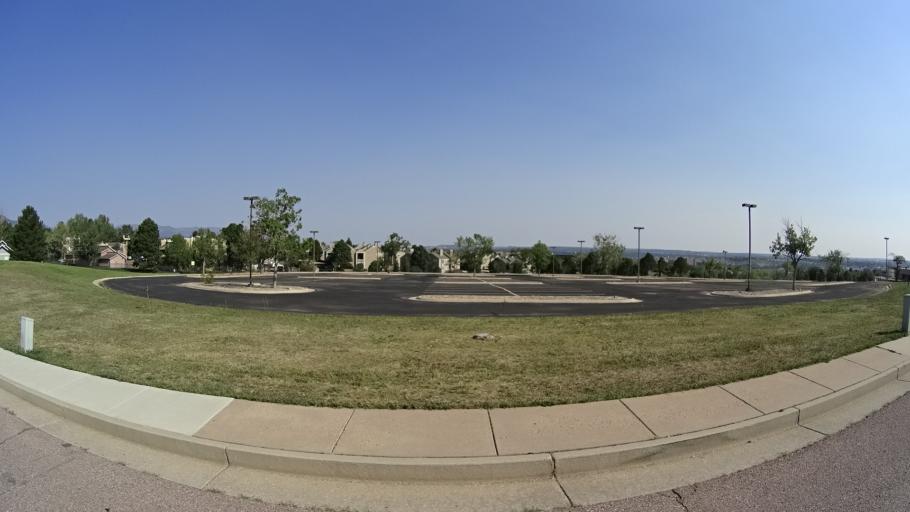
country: US
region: Colorado
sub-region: El Paso County
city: Stratmoor
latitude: 38.7814
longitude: -104.8080
